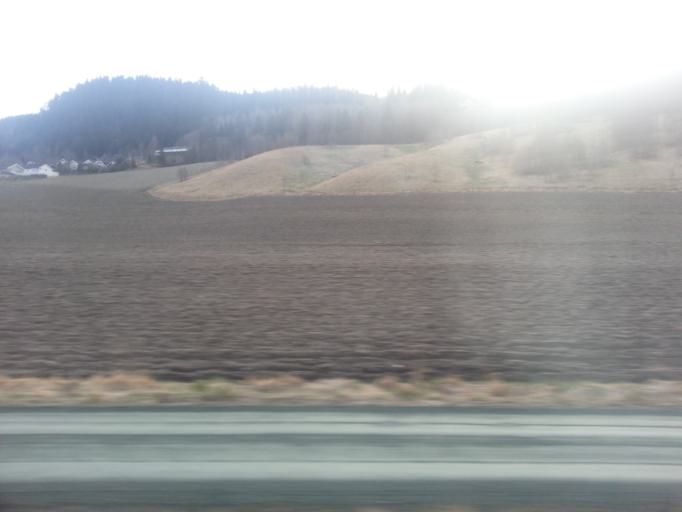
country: NO
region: Sor-Trondelag
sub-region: Melhus
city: Melhus
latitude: 63.2305
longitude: 10.2838
